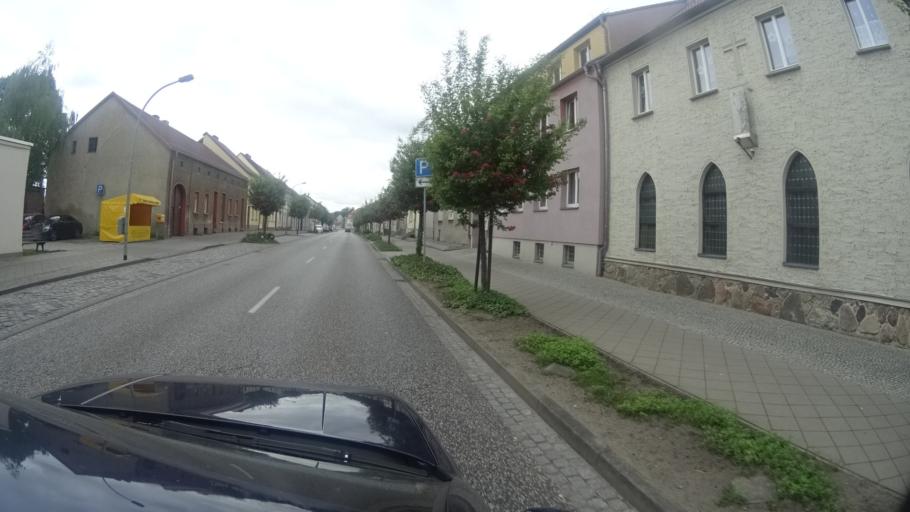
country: DE
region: Brandenburg
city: Fehrbellin
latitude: 52.8128
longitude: 12.7699
